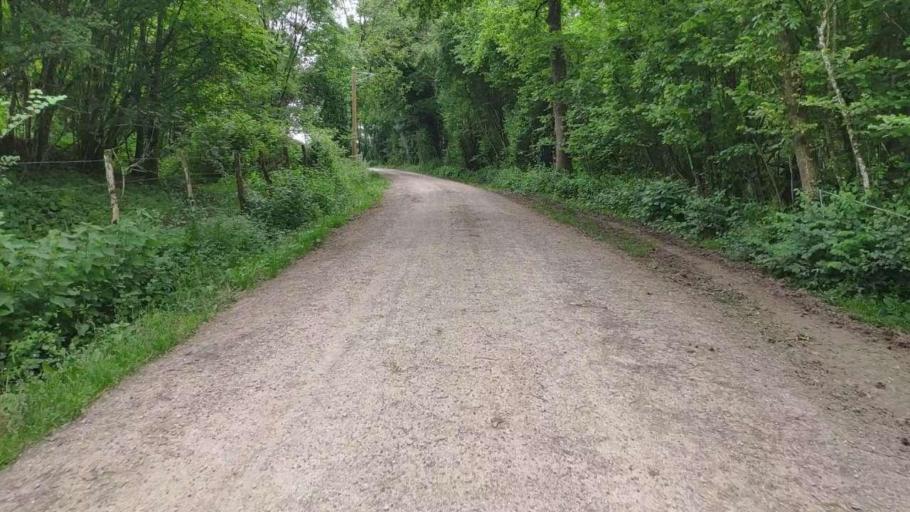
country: FR
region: Franche-Comte
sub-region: Departement du Jura
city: Montmorot
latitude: 46.7486
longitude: 5.5489
